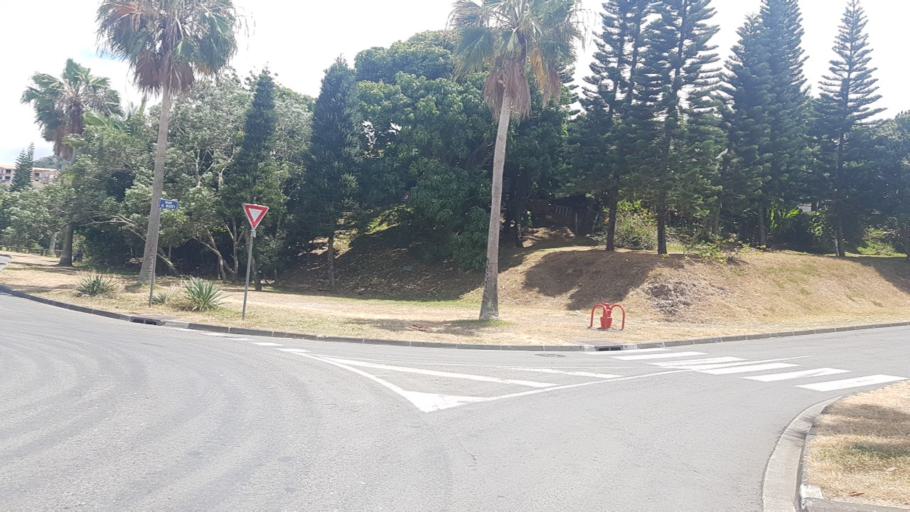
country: NC
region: South Province
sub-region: Dumbea
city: Dumbea
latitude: -22.2033
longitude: 166.4697
